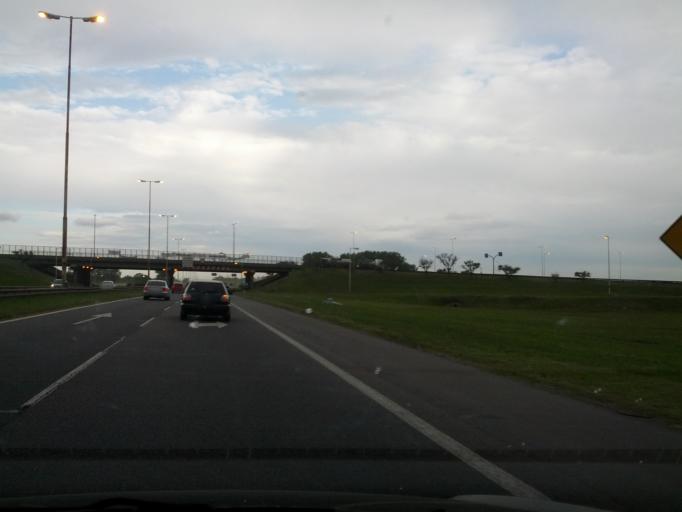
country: AR
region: Buenos Aires
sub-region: Partido de Lujan
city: Lujan
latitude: -34.5734
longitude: -59.0390
